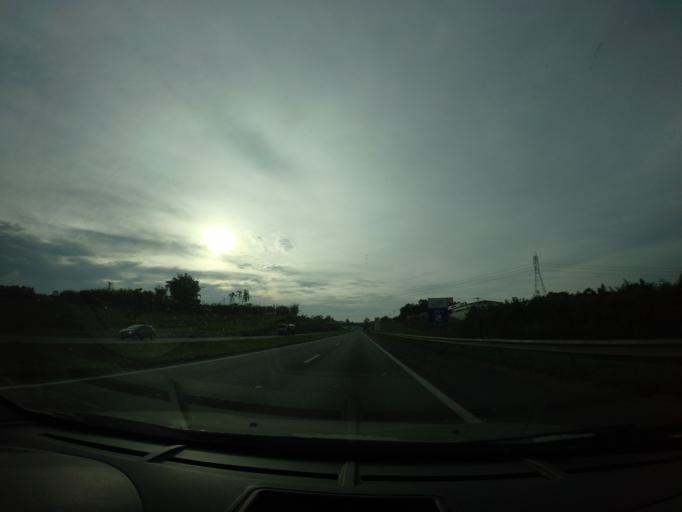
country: BR
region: Sao Paulo
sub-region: Jarinu
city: Jarinu
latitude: -23.0505
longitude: -46.6667
